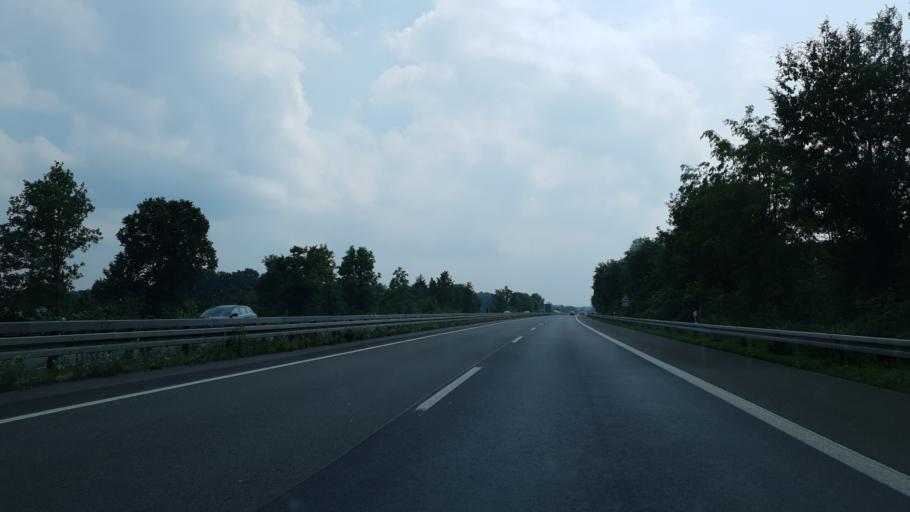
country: DE
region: North Rhine-Westphalia
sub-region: Regierungsbezirk Munster
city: Gescher
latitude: 51.9337
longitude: 7.0413
